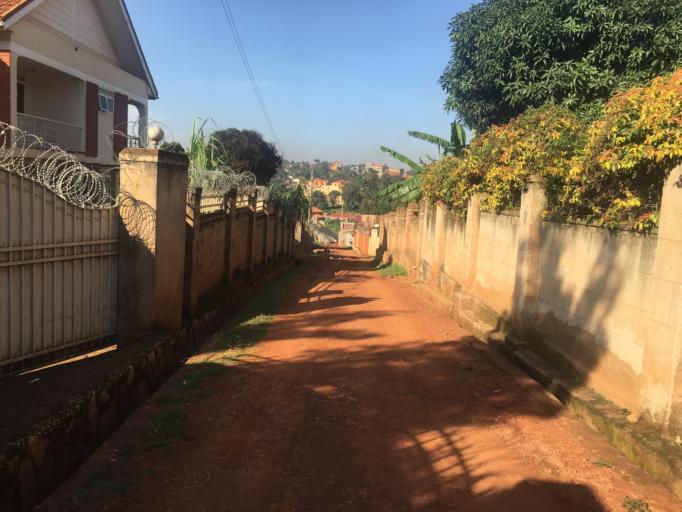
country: UG
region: Central Region
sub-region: Wakiso District
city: Kireka
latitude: 0.3589
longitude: 32.6245
